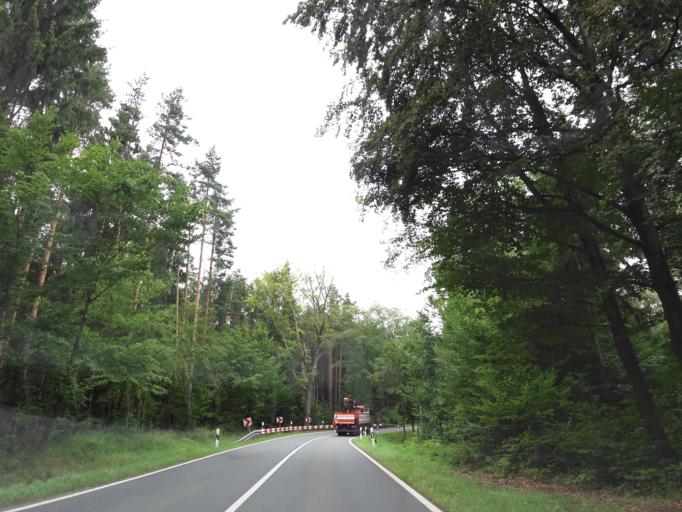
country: DE
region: Thuringia
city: Hainspitz
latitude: 50.9388
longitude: 11.8510
